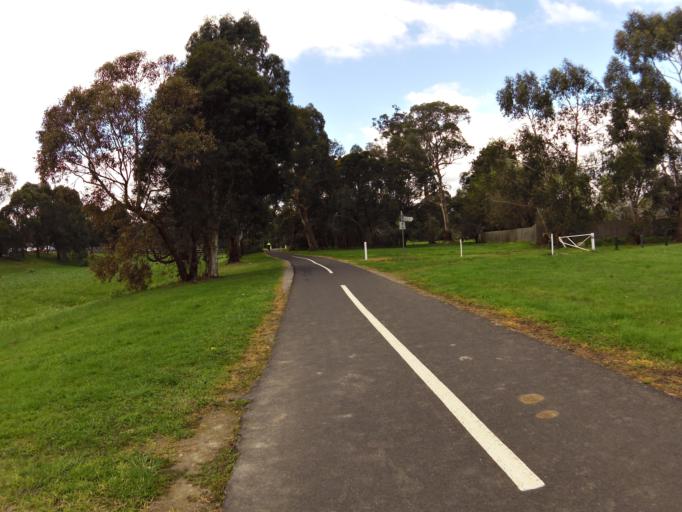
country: AU
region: Victoria
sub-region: Maroondah
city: Heathmont
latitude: -37.8367
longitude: 145.2547
